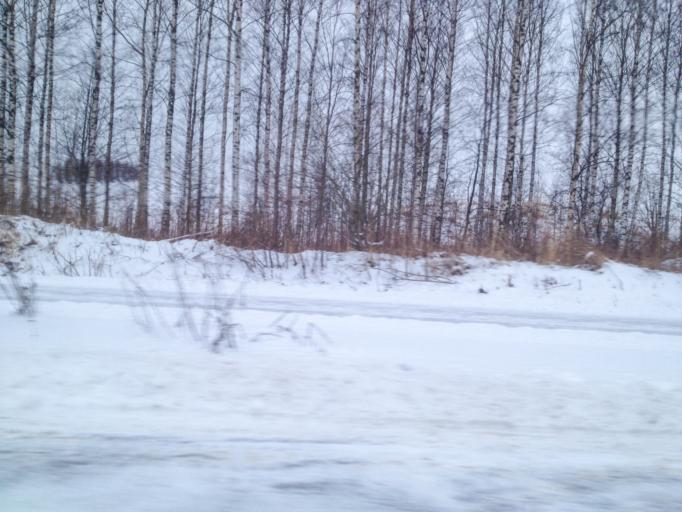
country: FI
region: Uusimaa
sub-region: Helsinki
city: Vantaa
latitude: 60.2108
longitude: 25.1729
